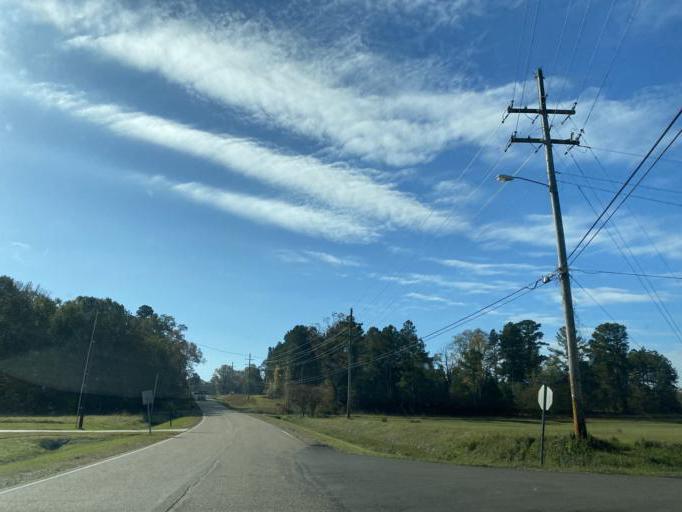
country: US
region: Mississippi
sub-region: Madison County
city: Madison
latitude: 32.4743
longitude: -90.1792
